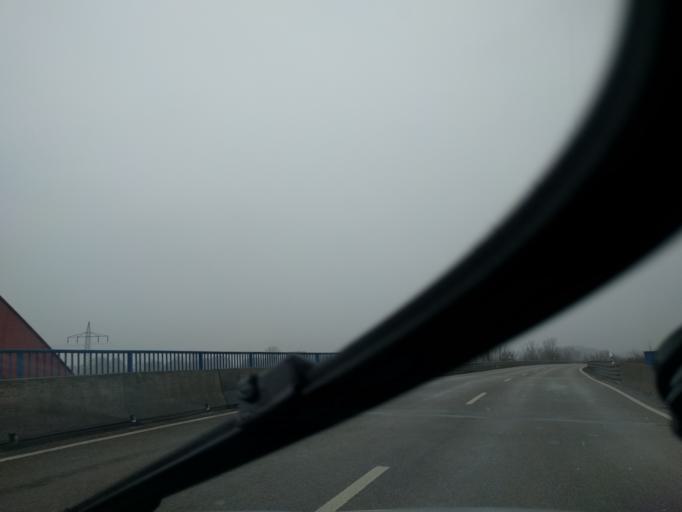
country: DE
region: Bavaria
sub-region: Swabia
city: Asbach-Baumenheim
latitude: 48.6932
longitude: 10.8000
